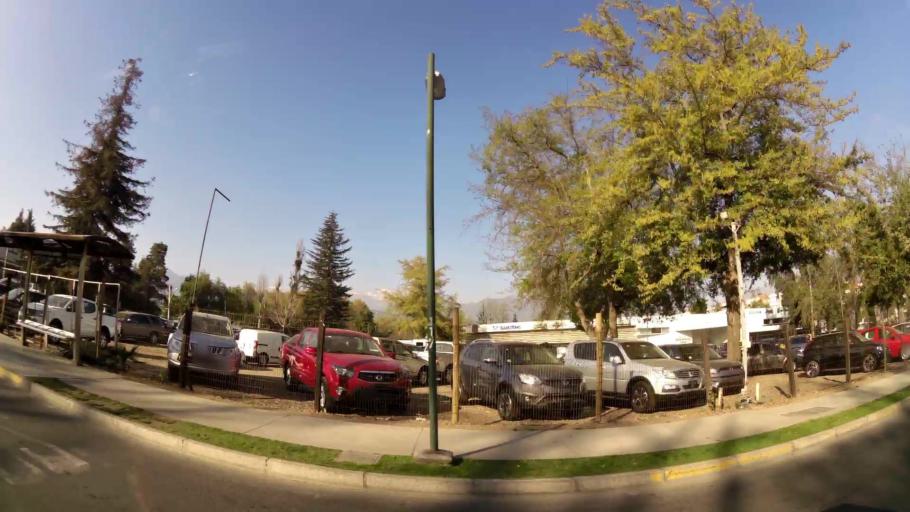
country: CL
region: Santiago Metropolitan
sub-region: Provincia de Santiago
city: Villa Presidente Frei, Nunoa, Santiago, Chile
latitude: -33.3533
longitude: -70.5183
